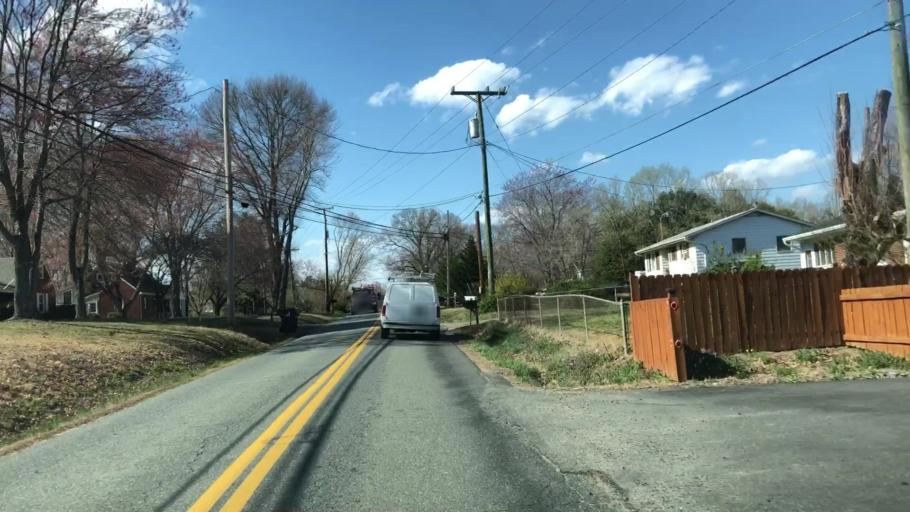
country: US
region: Virginia
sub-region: Stafford County
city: Falmouth
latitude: 38.3550
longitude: -77.4815
